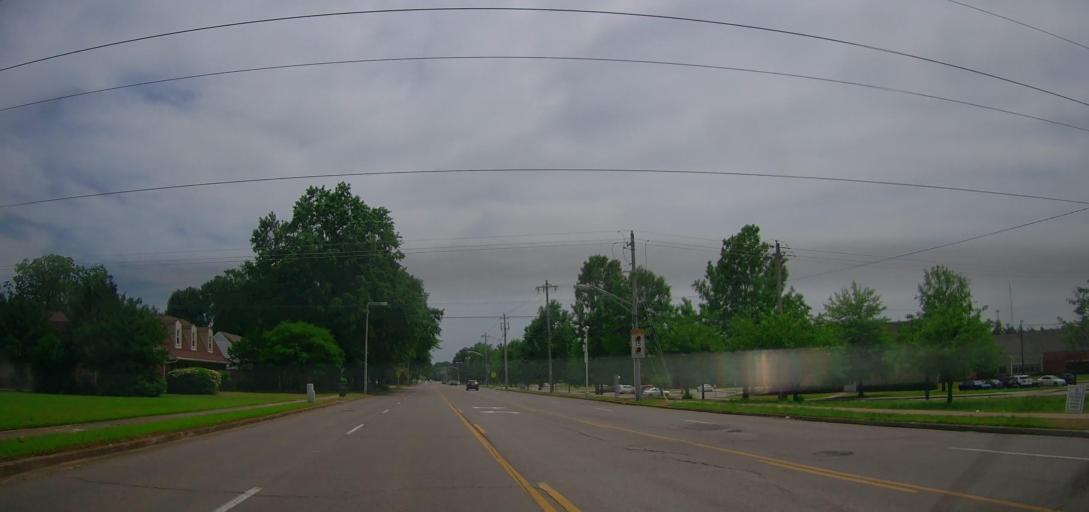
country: US
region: Tennessee
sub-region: Shelby County
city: Germantown
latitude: 35.0799
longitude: -89.8514
